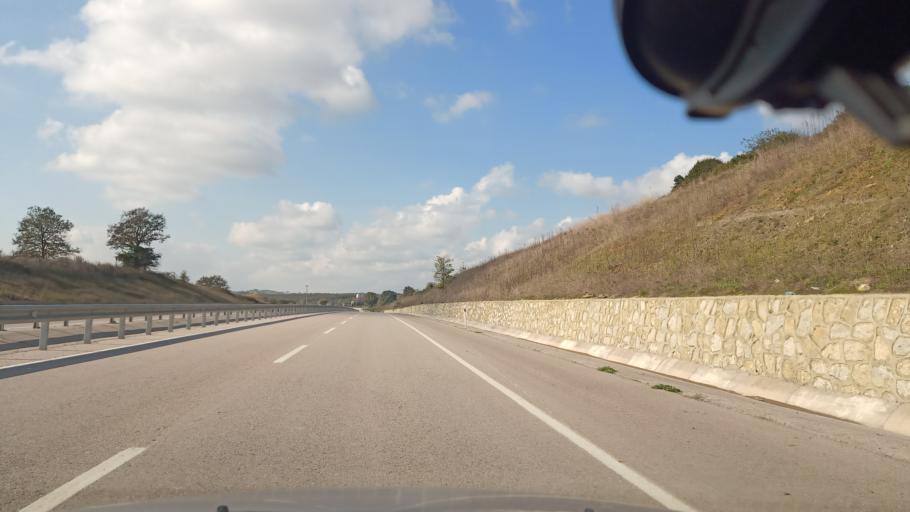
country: TR
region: Sakarya
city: Kaynarca
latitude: 41.0723
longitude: 30.3858
